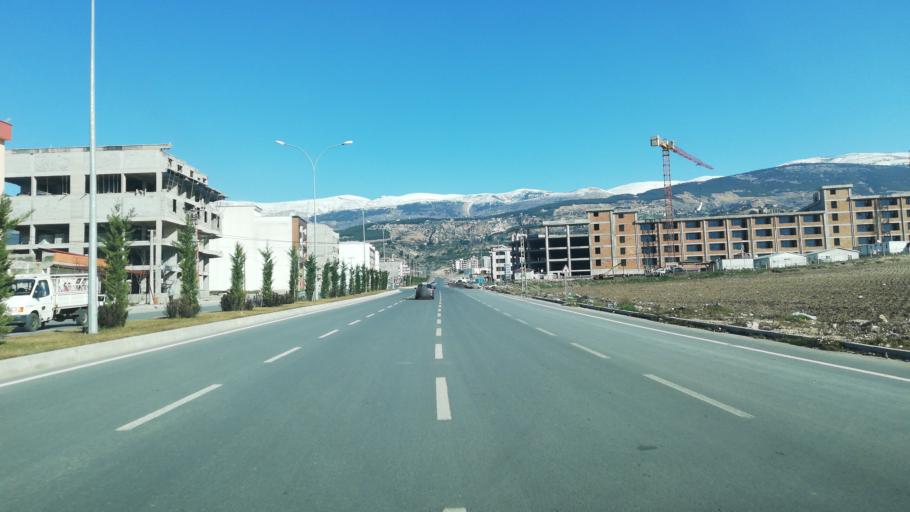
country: TR
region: Kahramanmaras
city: Kahramanmaras
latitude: 37.5736
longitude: 36.9746
